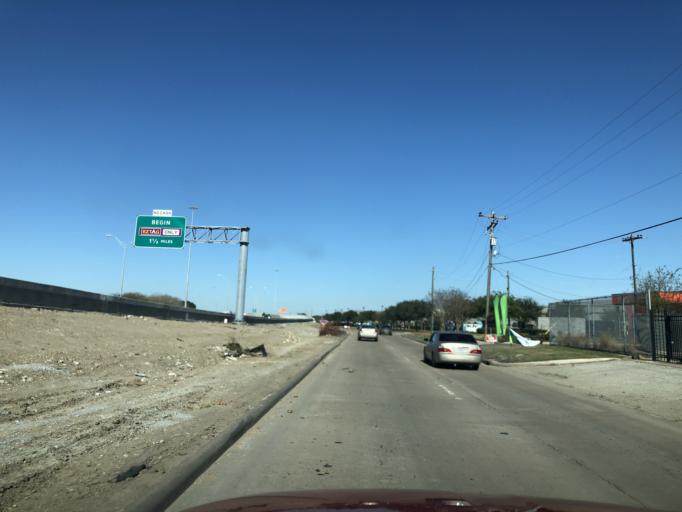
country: US
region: Texas
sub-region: Harris County
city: Deer Park
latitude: 29.6851
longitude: -95.1539
